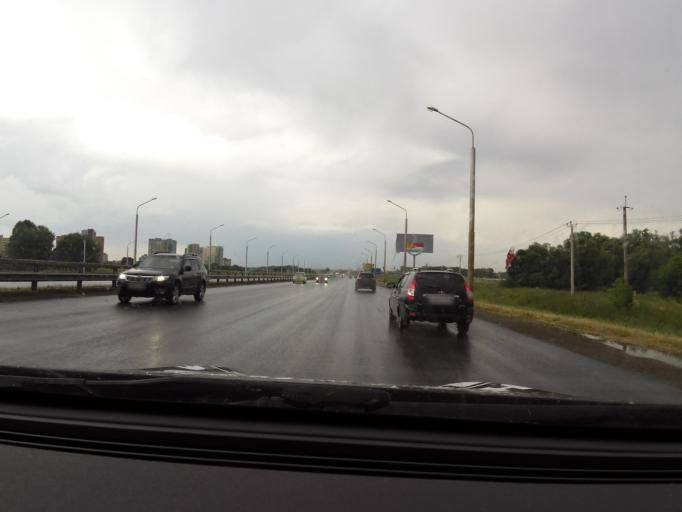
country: RU
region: Bashkortostan
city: Mikhaylovka
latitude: 54.7979
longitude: 55.8824
